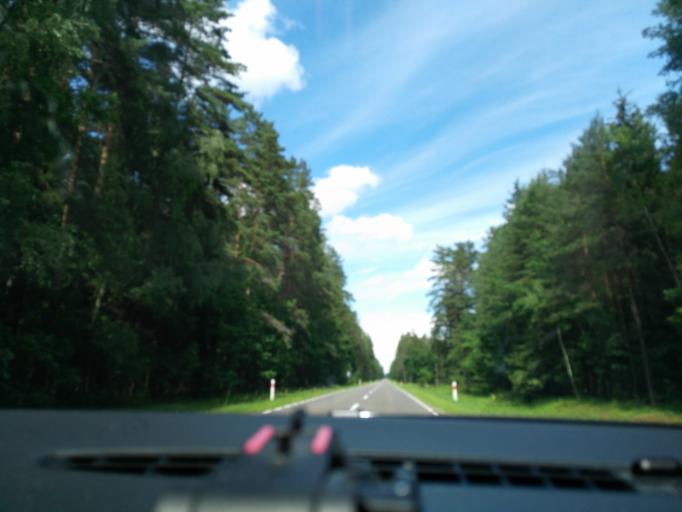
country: PL
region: Podlasie
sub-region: Powiat sejnenski
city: Sejny
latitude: 53.9859
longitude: 23.2985
